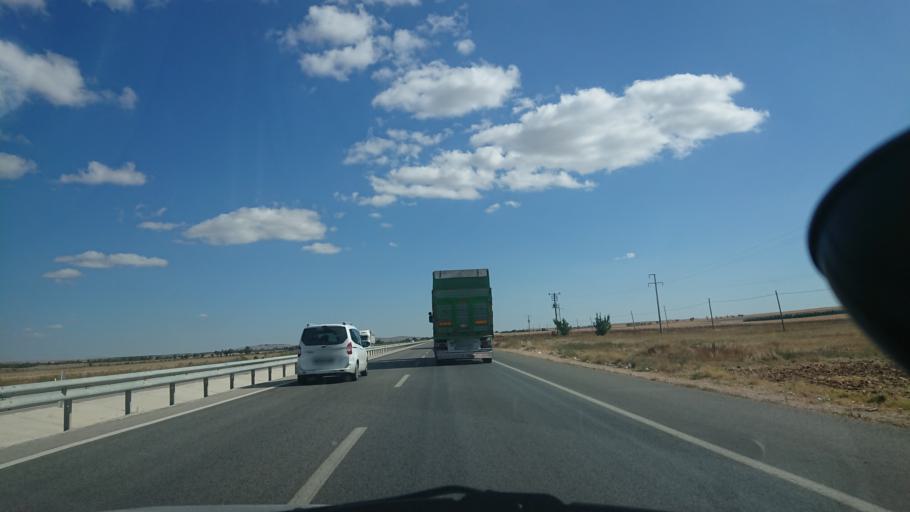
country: TR
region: Eskisehir
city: Mahmudiye
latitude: 39.5519
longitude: 30.9257
